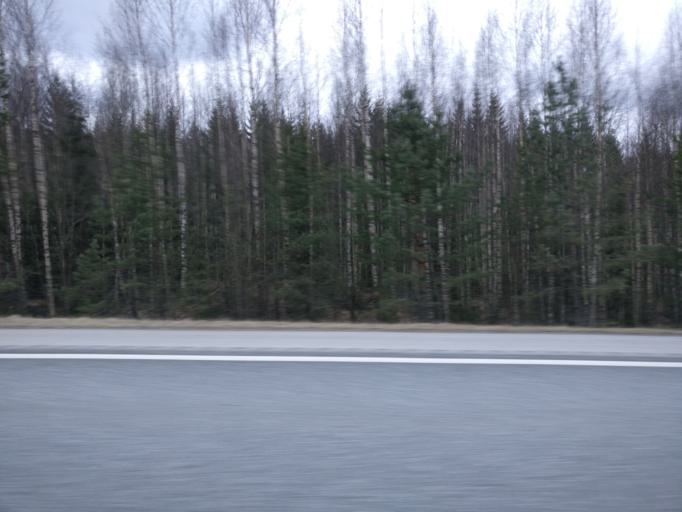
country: FI
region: Haeme
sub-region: Haemeenlinna
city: Janakkala
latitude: 60.8577
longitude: 24.5911
